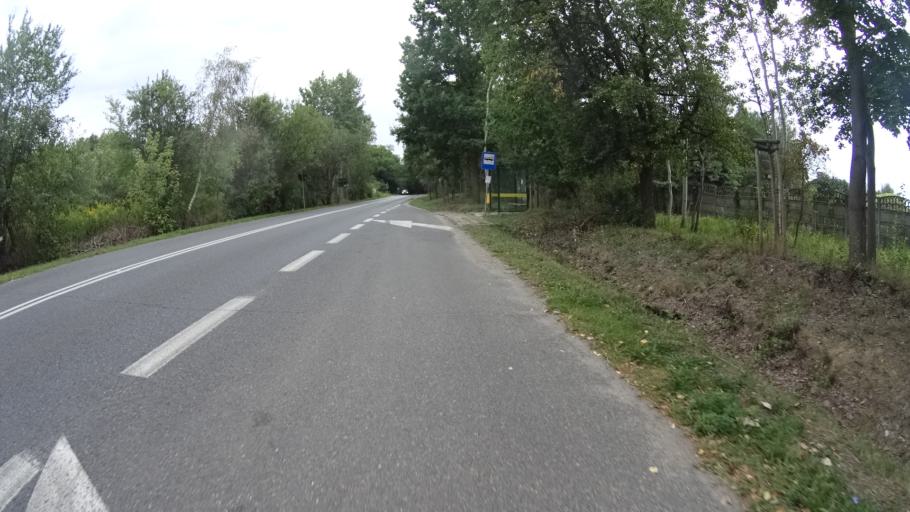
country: PL
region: Masovian Voivodeship
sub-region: Powiat pruszkowski
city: Granica
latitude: 52.1248
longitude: 20.7987
